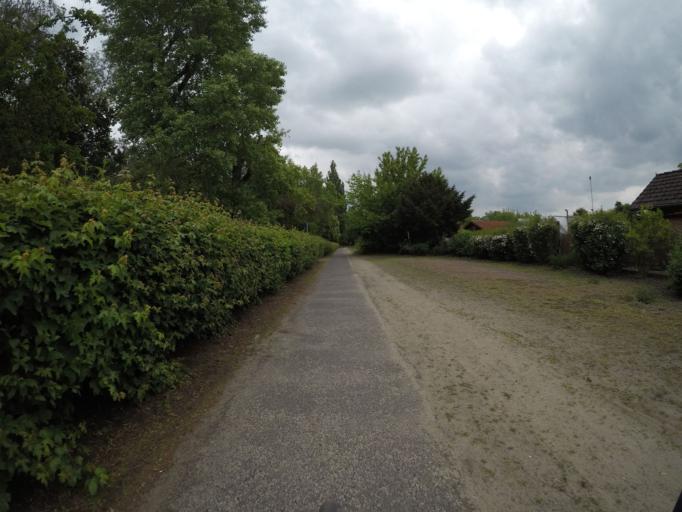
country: DE
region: Berlin
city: Reinickendorf
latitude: 52.5768
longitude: 13.3439
